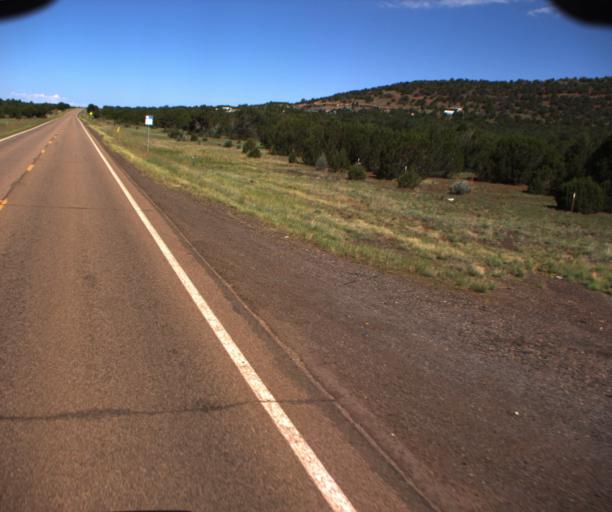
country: US
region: Arizona
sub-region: Navajo County
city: Pinetop-Lakeside
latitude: 34.2759
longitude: -109.7839
